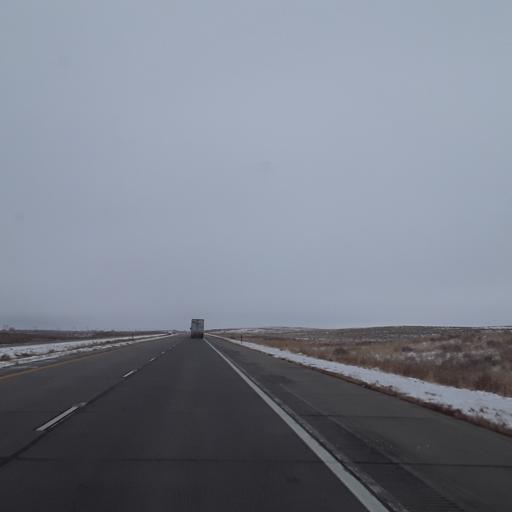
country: US
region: Colorado
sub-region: Logan County
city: Sterling
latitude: 40.5681
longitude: -103.2060
